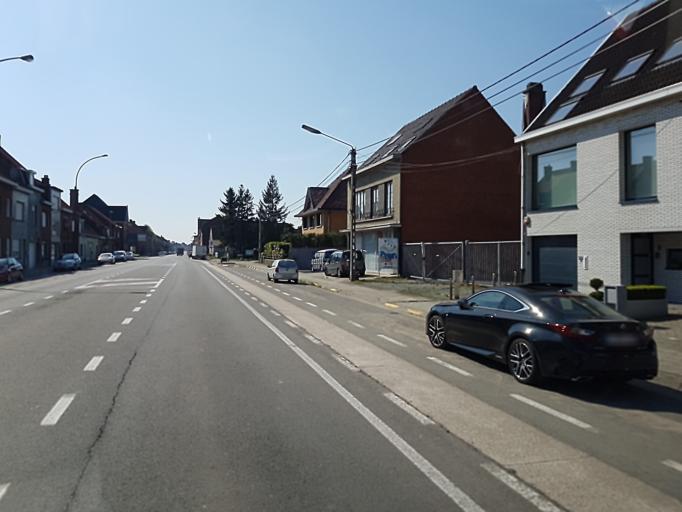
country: BE
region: Flanders
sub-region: Provincie West-Vlaanderen
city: Menen
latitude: 50.8122
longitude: 3.1212
